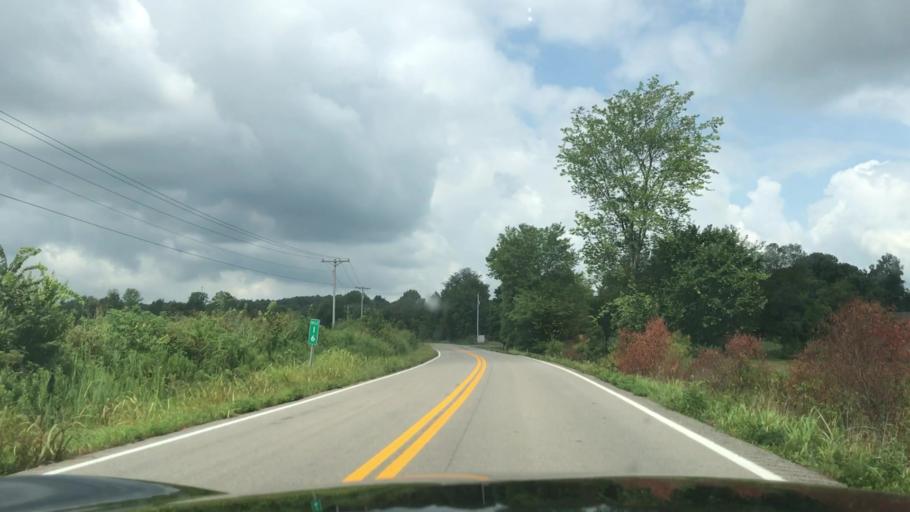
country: US
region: Kentucky
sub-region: Muhlenberg County
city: Central City
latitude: 37.2044
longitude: -87.0157
